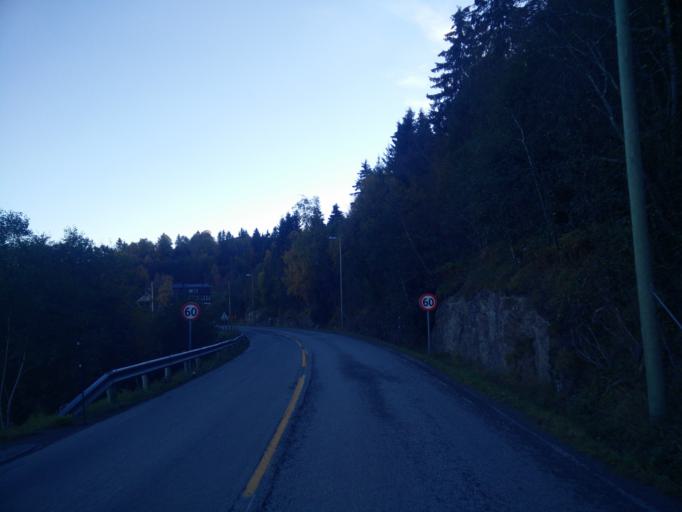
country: NO
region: Sor-Trondelag
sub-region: Skaun
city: Borsa
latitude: 63.3402
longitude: 10.0568
